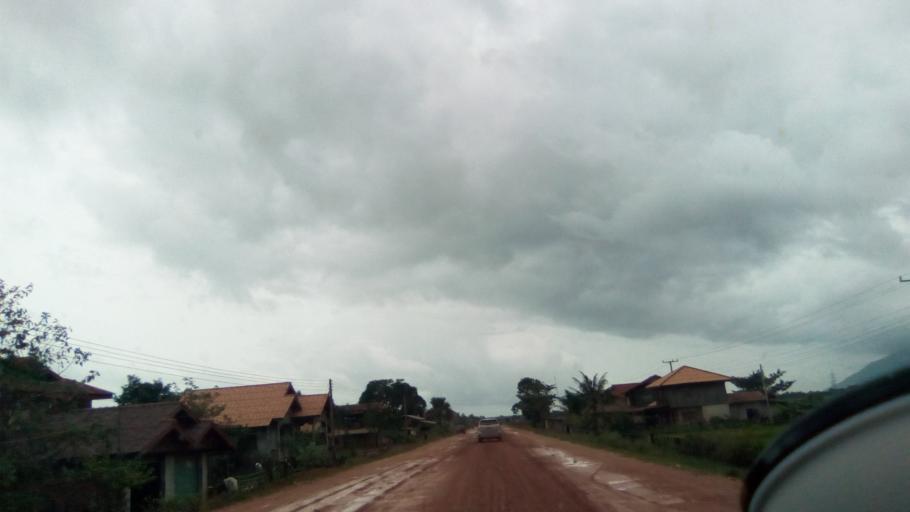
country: LA
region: Attapu
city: Attapu
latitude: 14.7400
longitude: 106.6899
